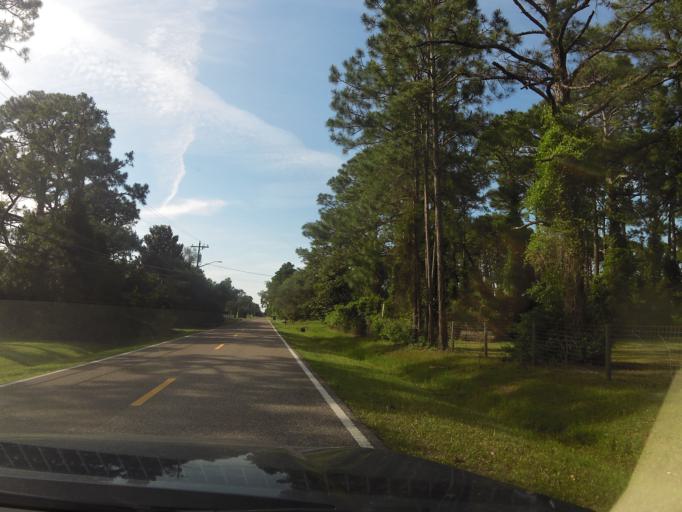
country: US
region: Florida
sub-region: Nassau County
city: Fernandina Beach
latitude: 30.5144
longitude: -81.4778
